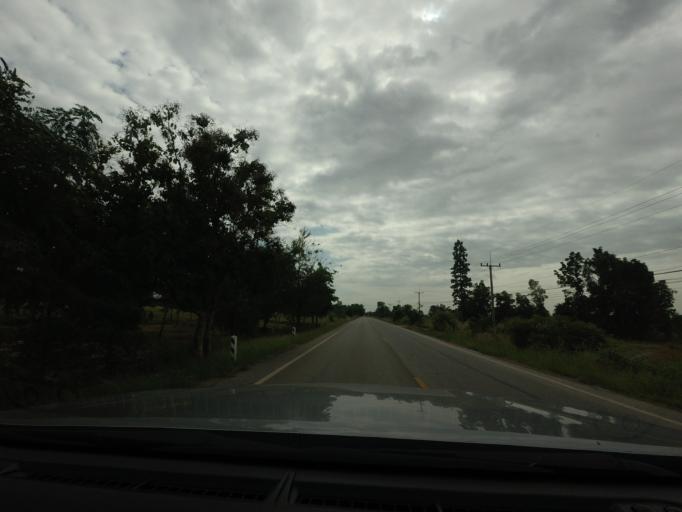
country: TH
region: Phitsanulok
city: Noen Maprang
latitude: 16.6319
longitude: 100.6180
